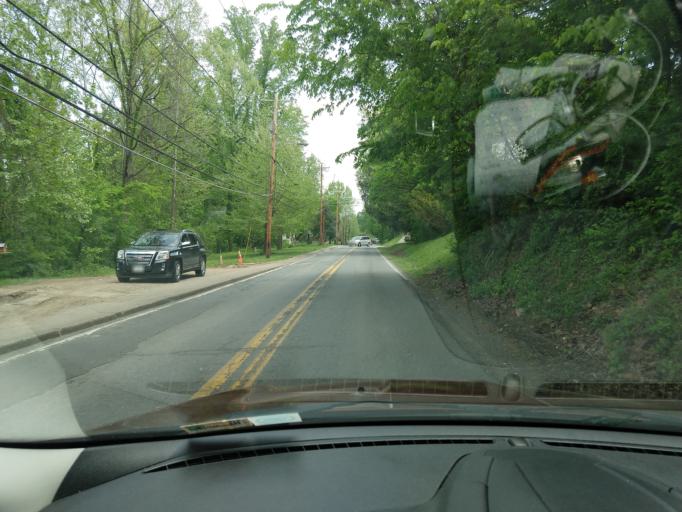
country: US
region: West Virginia
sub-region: Kanawha County
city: Saint Albans
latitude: 38.3763
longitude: -81.8007
